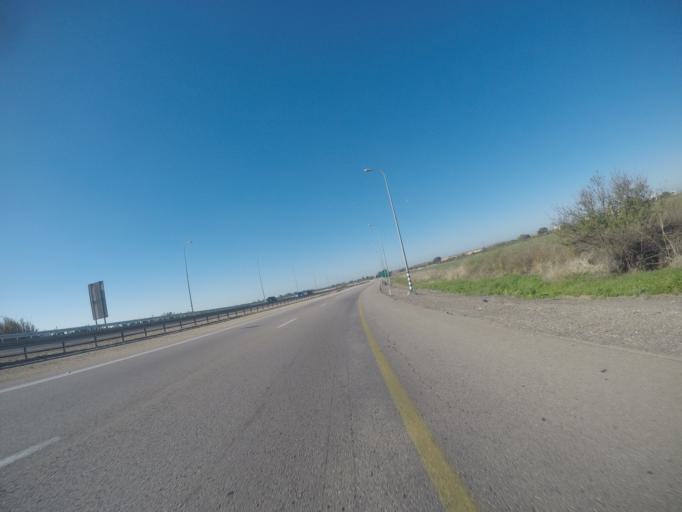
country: IL
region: Southern District
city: Ashdod
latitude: 31.7515
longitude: 34.6597
